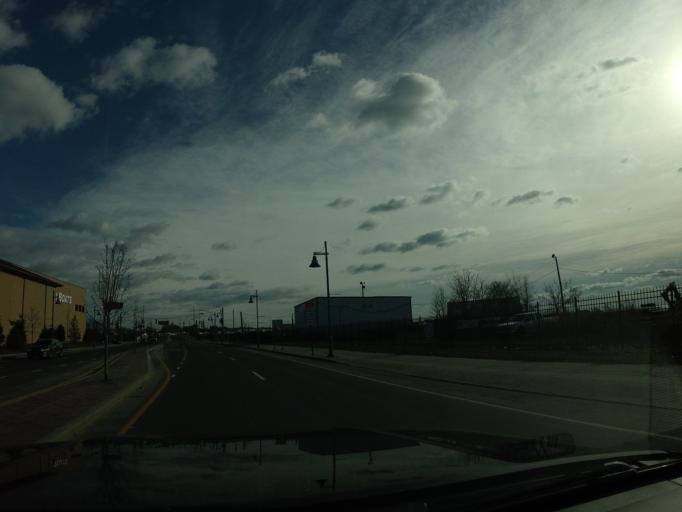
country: US
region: Connecticut
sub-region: Fairfield County
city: Bridgeport
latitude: 41.1771
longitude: -73.1789
